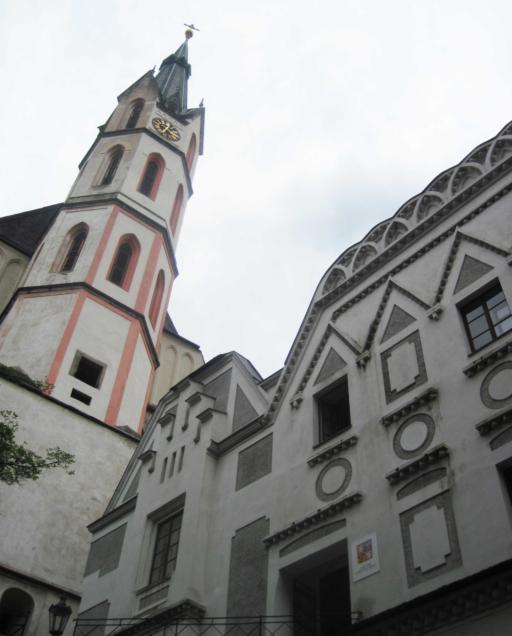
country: CZ
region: Jihocesky
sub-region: Okres Cesky Krumlov
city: Cesky Krumlov
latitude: 48.8101
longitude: 14.3153
